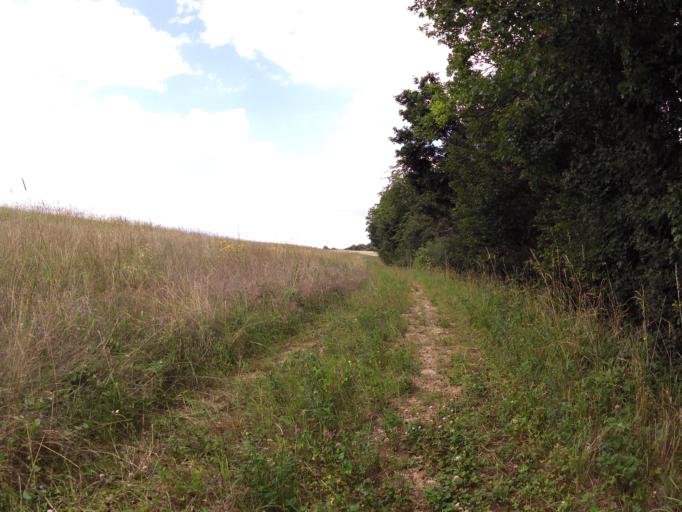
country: DE
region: Bavaria
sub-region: Regierungsbezirk Unterfranken
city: Thungersheim
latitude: 49.8884
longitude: 9.8696
